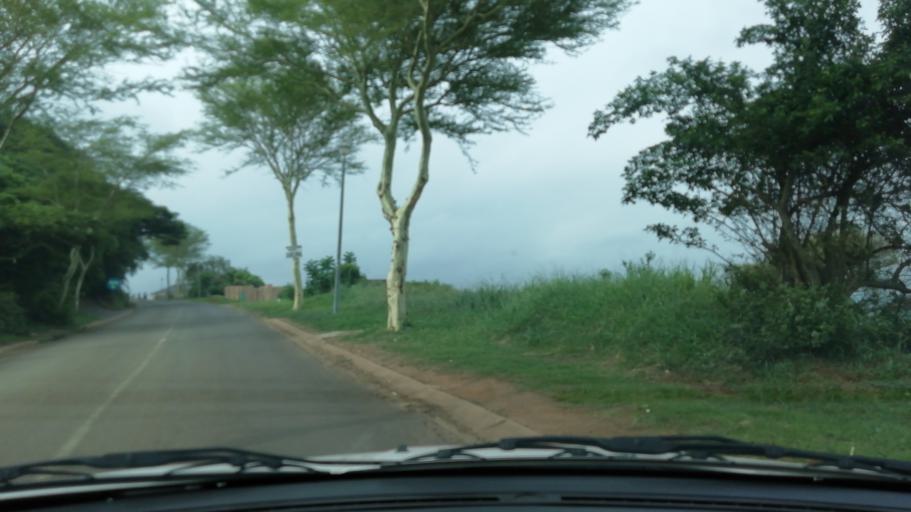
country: ZA
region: KwaZulu-Natal
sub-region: uThungulu District Municipality
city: Empangeni
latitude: -28.7419
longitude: 31.8802
